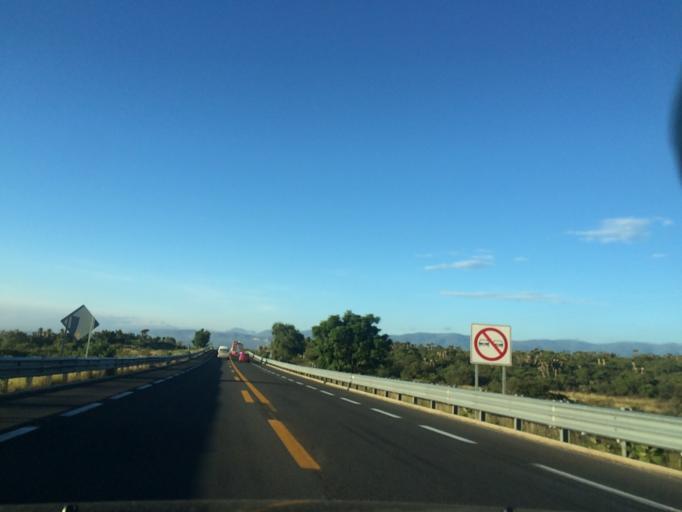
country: MX
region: Puebla
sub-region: Tehuacan
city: Magdalena Cuayucatepec
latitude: 18.5738
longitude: -97.4643
